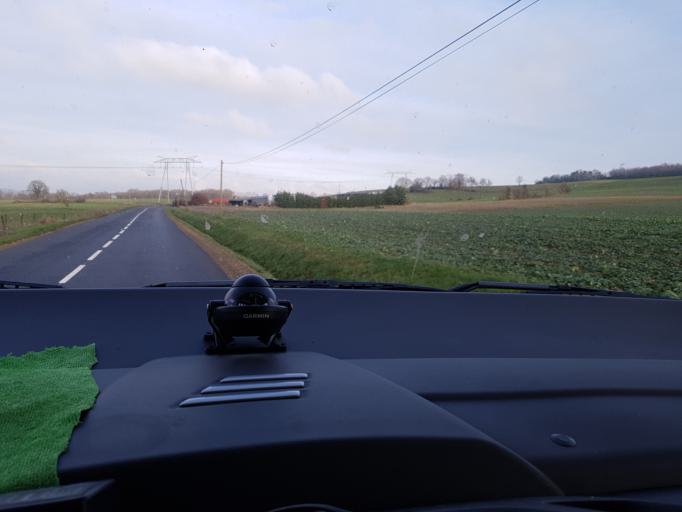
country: FR
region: Champagne-Ardenne
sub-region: Departement des Ardennes
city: Tournes
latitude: 49.7525
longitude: 4.6173
